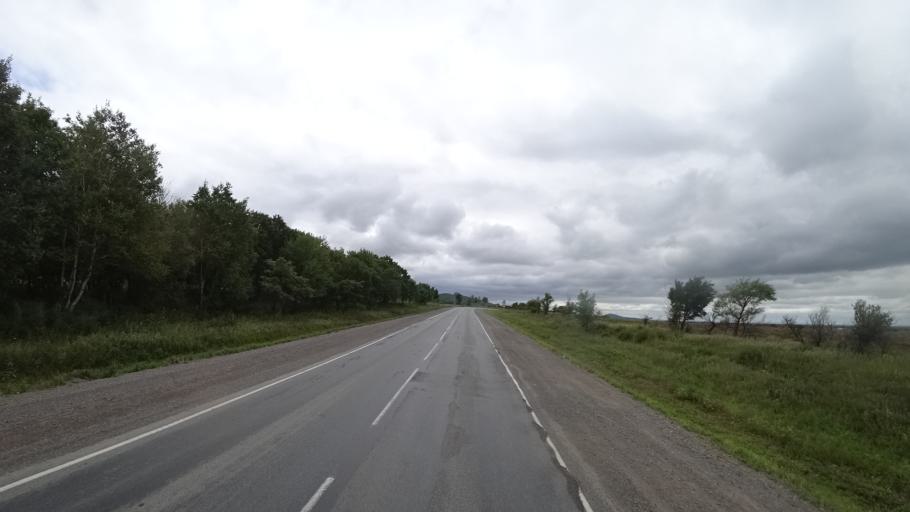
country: RU
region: Primorskiy
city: Chernigovka
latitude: 44.3182
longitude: 132.5647
